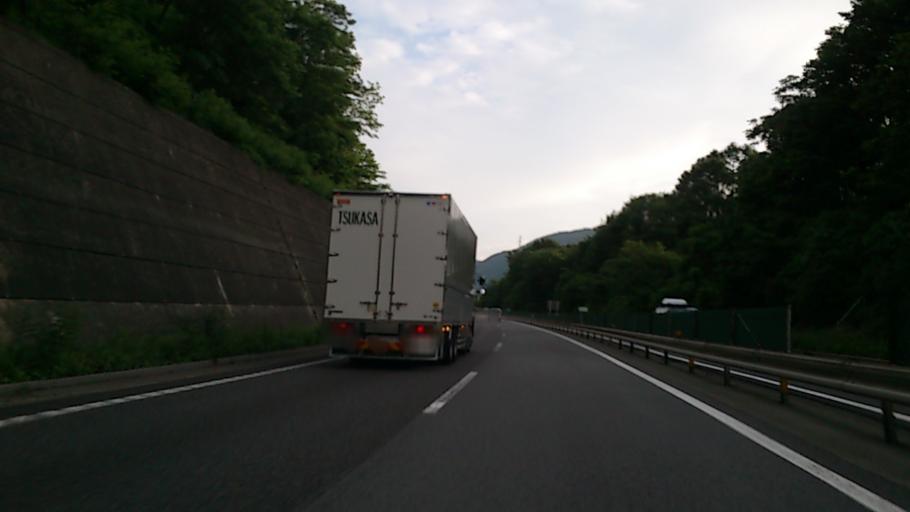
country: JP
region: Nagano
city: Okaya
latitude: 36.0343
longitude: 138.0247
